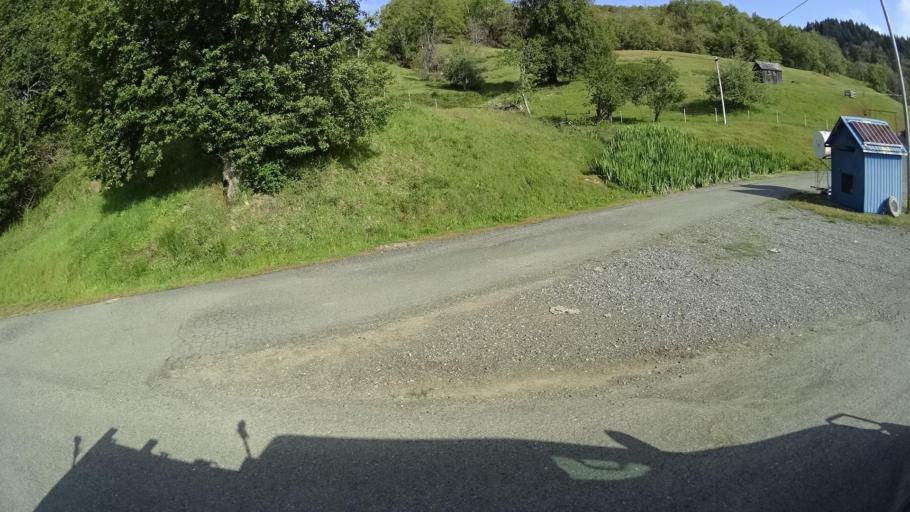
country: US
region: California
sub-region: Humboldt County
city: Hydesville
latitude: 40.6396
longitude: -123.8931
